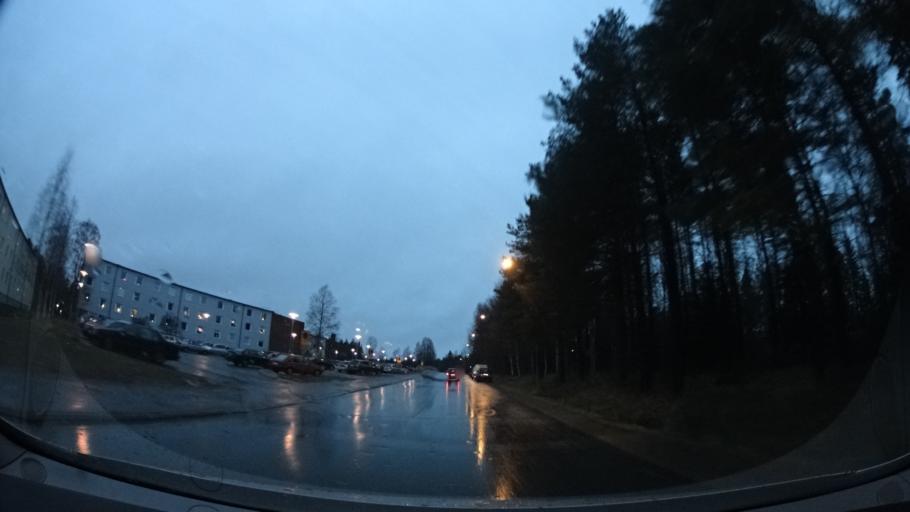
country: SE
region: Vaesterbotten
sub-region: Skelleftea Kommun
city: Skelleftea
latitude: 64.7544
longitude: 21.0147
